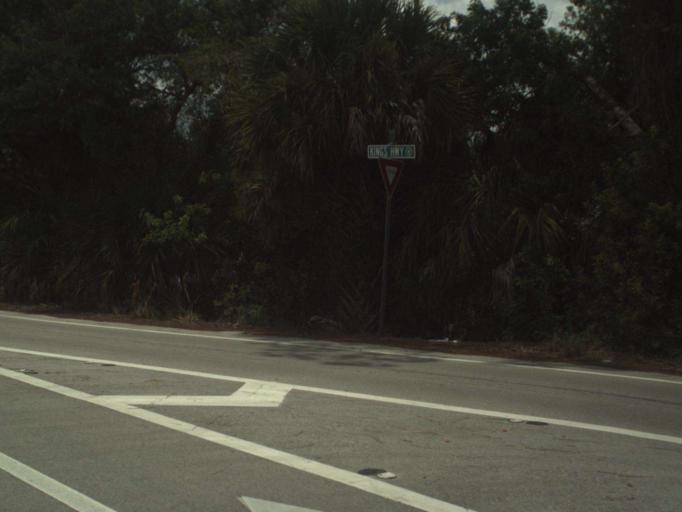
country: US
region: Florida
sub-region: Saint Lucie County
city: Lakewood Park
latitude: 27.5233
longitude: -80.3982
